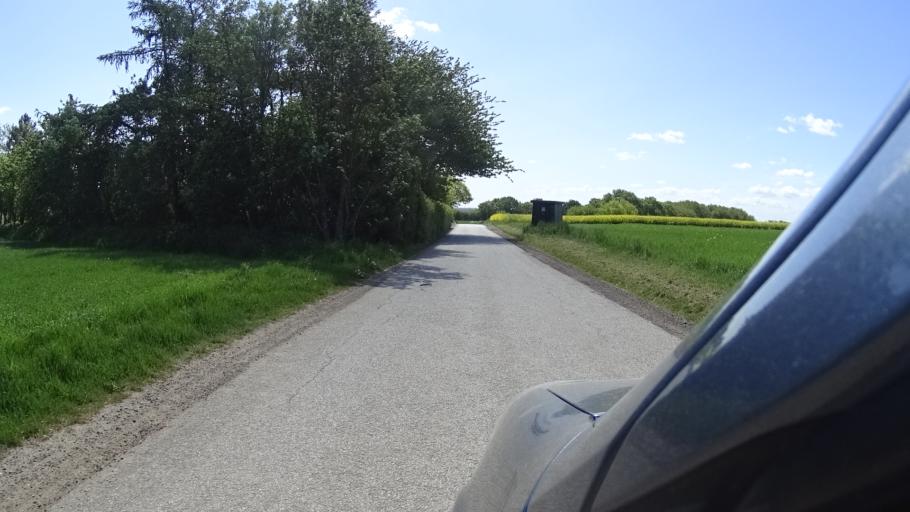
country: DK
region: South Denmark
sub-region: Vejle Kommune
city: Borkop
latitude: 55.6264
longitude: 9.6476
